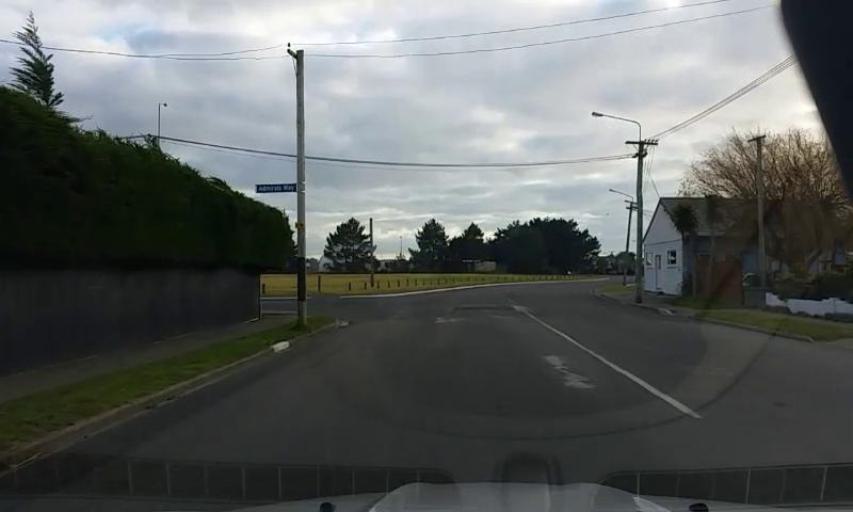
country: NZ
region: Canterbury
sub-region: Christchurch City
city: Christchurch
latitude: -43.5150
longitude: 172.7292
